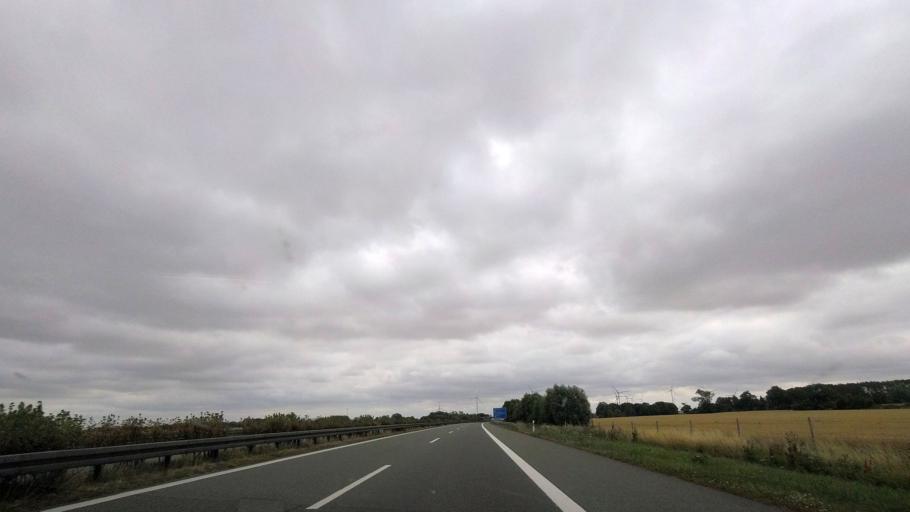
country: DE
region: Mecklenburg-Vorpommern
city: Dersekow
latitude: 54.0749
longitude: 13.1983
